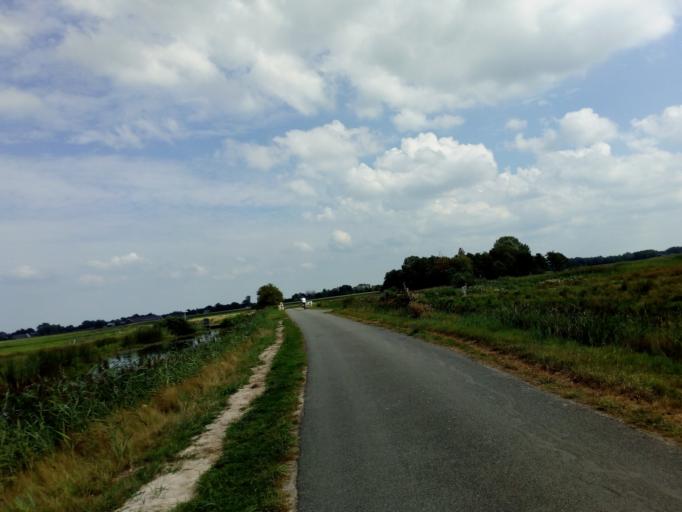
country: NL
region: Friesland
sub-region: Gemeente Smallingerland
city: Oudega
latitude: 53.1203
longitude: 5.9605
